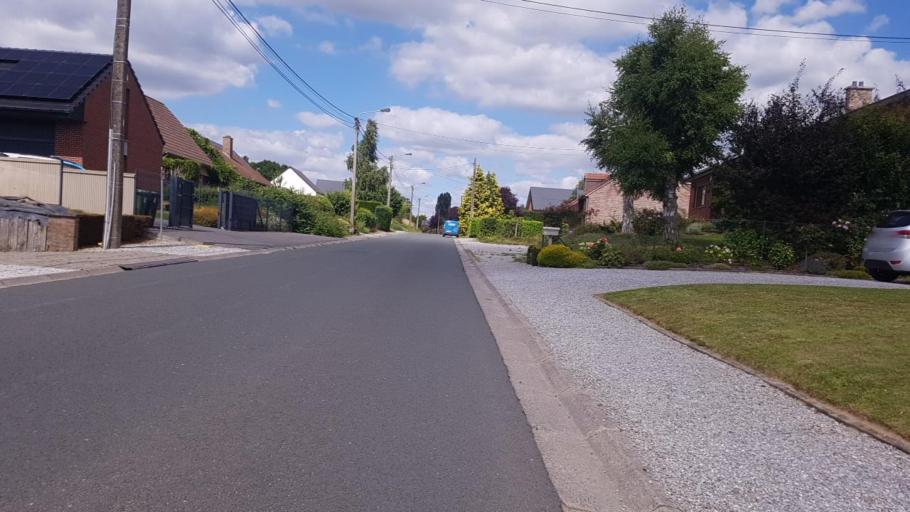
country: BE
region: Wallonia
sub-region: Province de Namur
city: Walcourt
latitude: 50.3343
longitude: 4.3891
